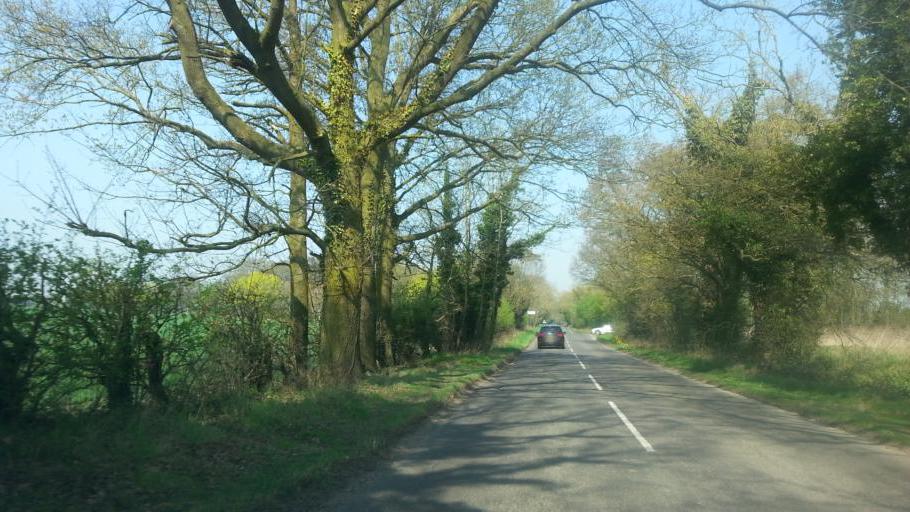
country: GB
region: England
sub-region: Suffolk
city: Thurston
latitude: 52.2420
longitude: 0.8223
